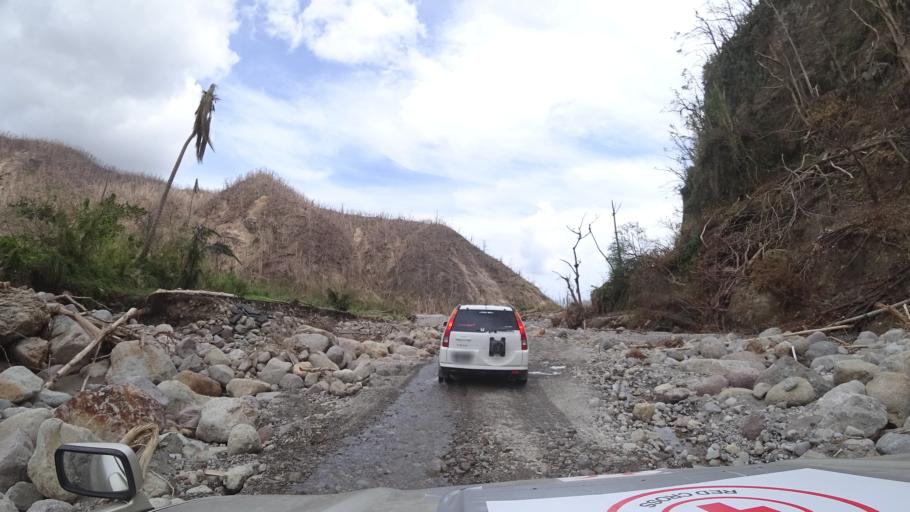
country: DM
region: Saint Patrick
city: Berekua
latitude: 15.2549
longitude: -61.3179
